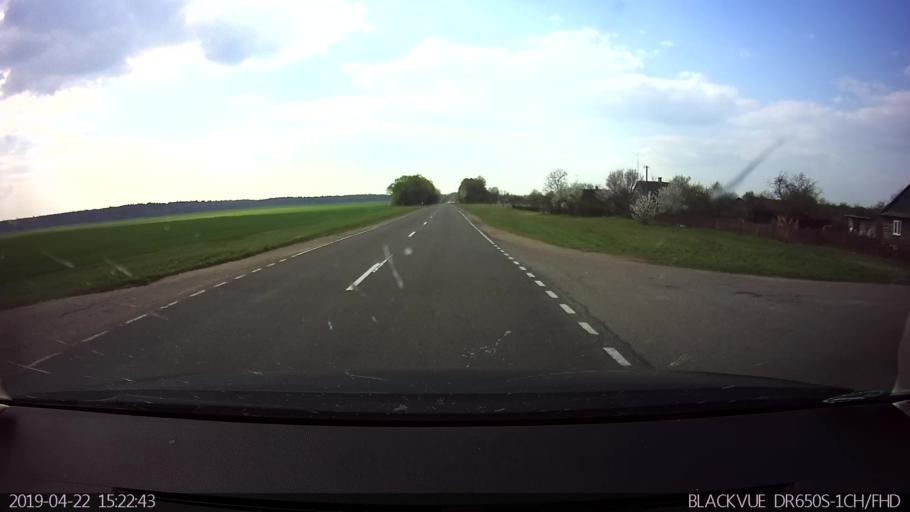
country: BY
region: Brest
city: Vysokaye
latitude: 52.3514
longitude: 23.4403
